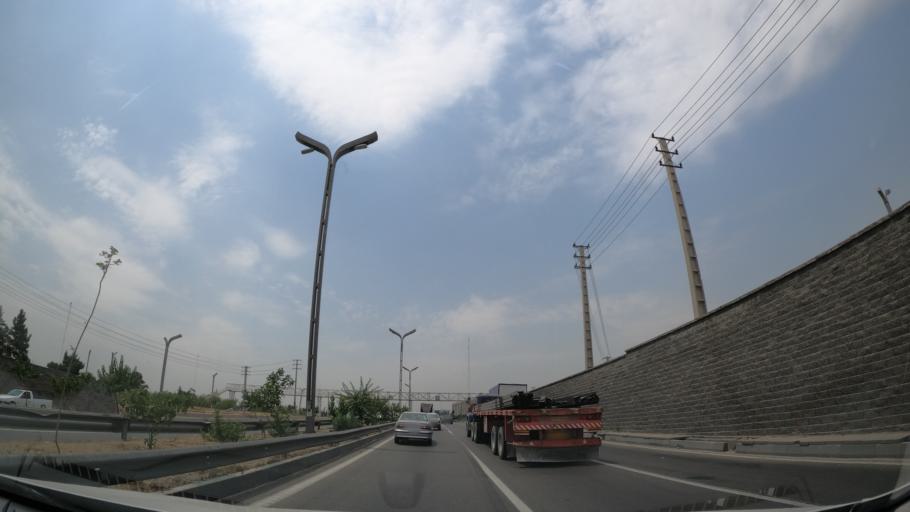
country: IR
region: Tehran
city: Shahr-e Qods
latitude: 35.7038
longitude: 51.1826
